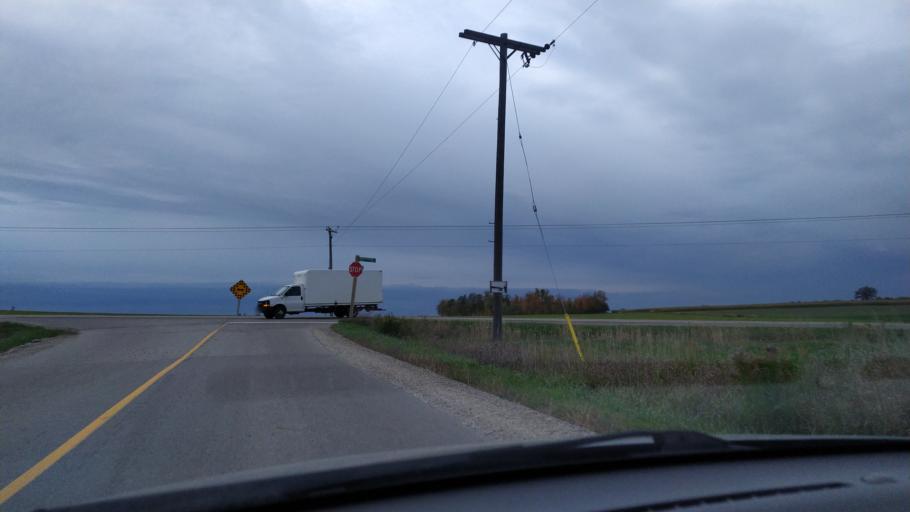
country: CA
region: Ontario
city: Waterloo
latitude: 43.5138
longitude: -80.7542
